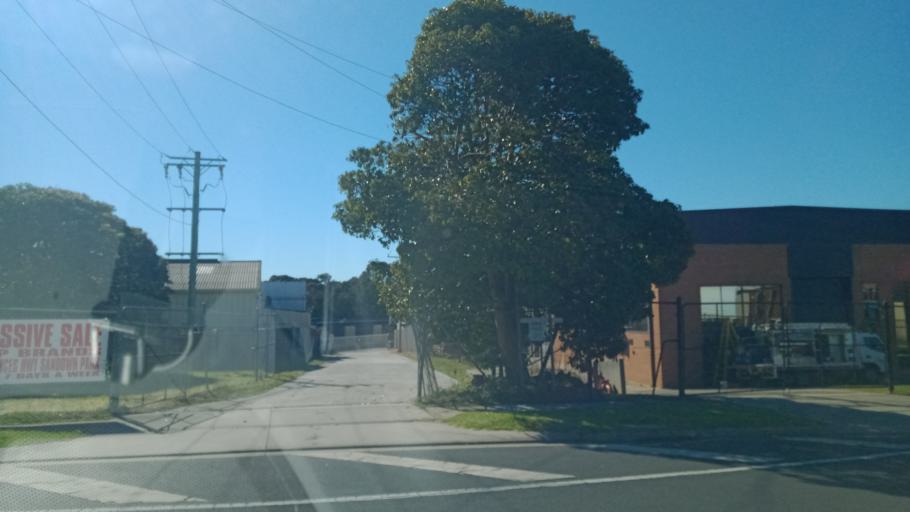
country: AU
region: Victoria
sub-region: Greater Dandenong
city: Springvale
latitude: -37.9410
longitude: 145.1704
